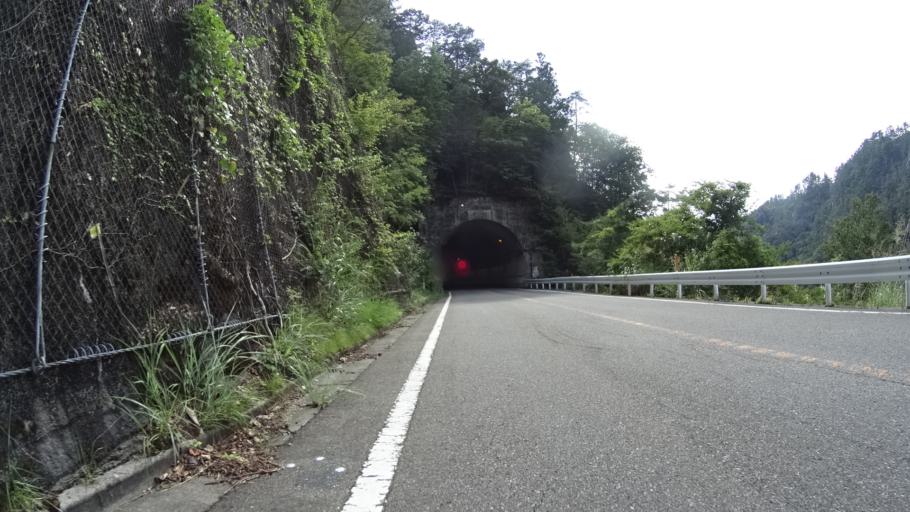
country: JP
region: Yamanashi
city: Kofu-shi
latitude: 35.7317
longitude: 138.5603
